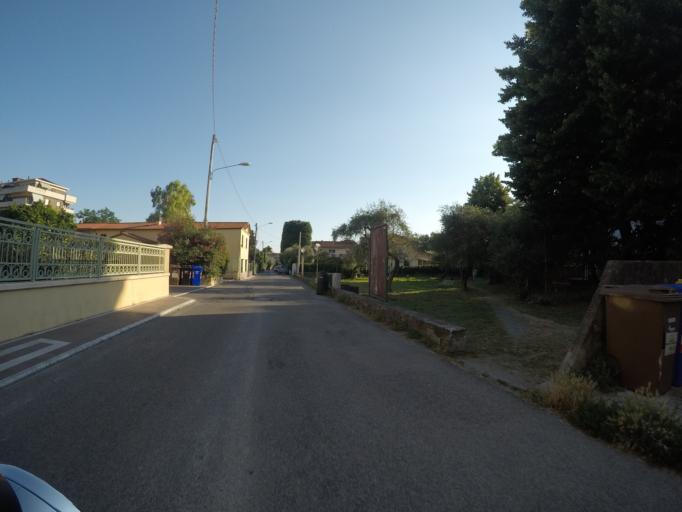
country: IT
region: Tuscany
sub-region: Provincia di Massa-Carrara
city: Massa
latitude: 44.0308
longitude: 10.1364
